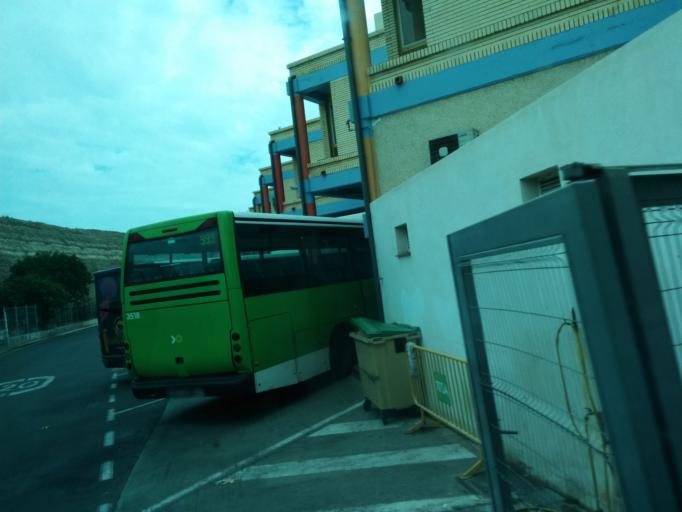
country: ES
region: Canary Islands
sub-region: Provincia de Santa Cruz de Tenerife
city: Playa de las Americas
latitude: 28.0720
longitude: -16.7281
